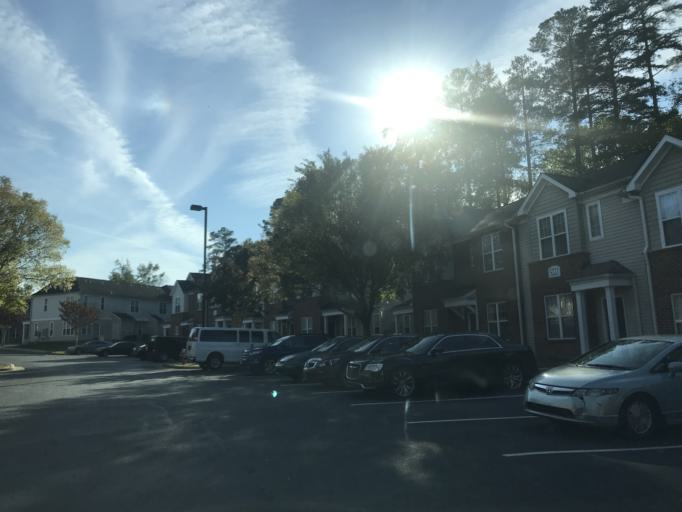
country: US
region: North Carolina
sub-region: Wake County
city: Wake Forest
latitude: 35.9018
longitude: -78.5531
